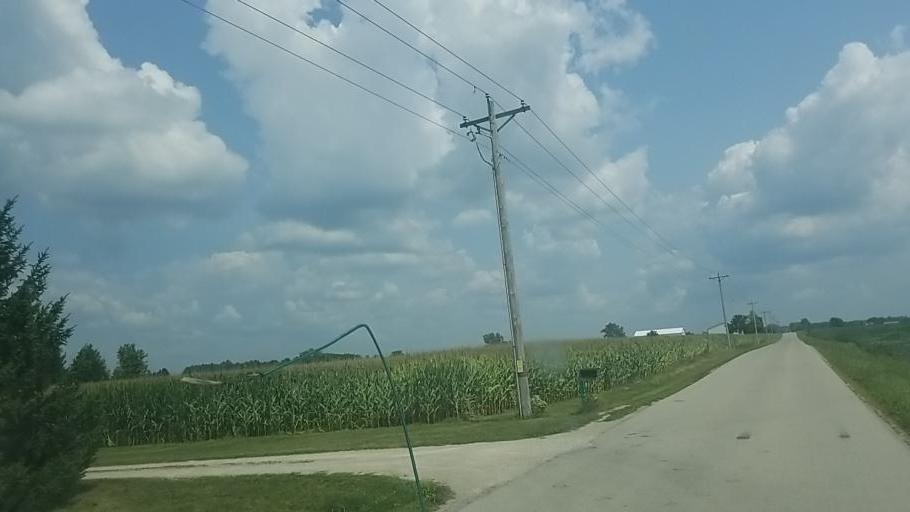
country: US
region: Ohio
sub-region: Wyandot County
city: Upper Sandusky
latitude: 40.9209
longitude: -83.1650
